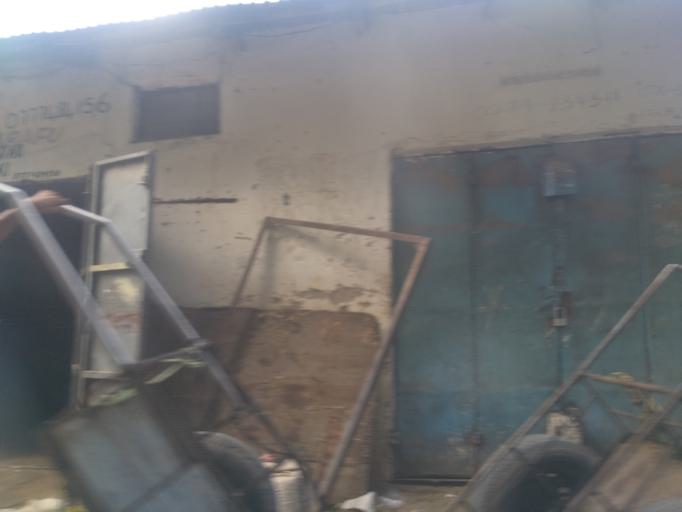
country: TZ
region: Zanzibar Urban/West
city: Zanzibar
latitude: -6.1633
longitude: 39.2110
